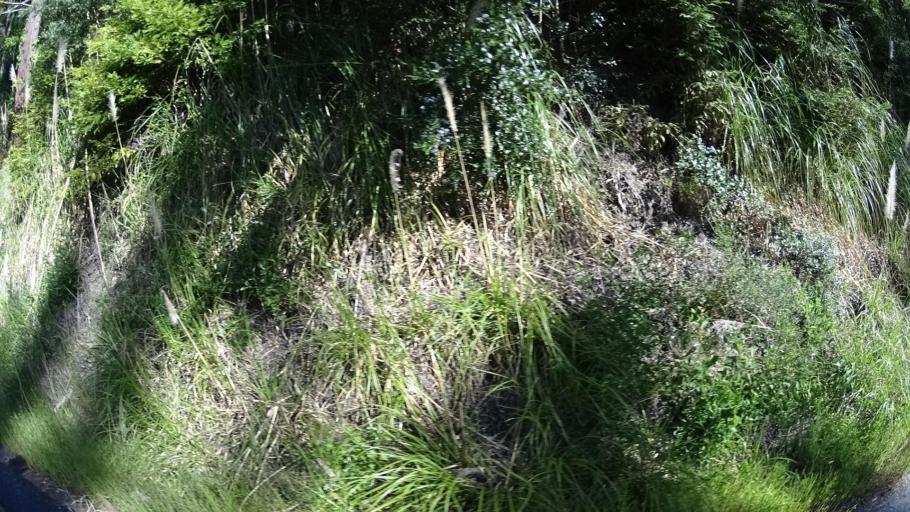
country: US
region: California
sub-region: Humboldt County
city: Rio Dell
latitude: 40.4622
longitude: -124.0558
